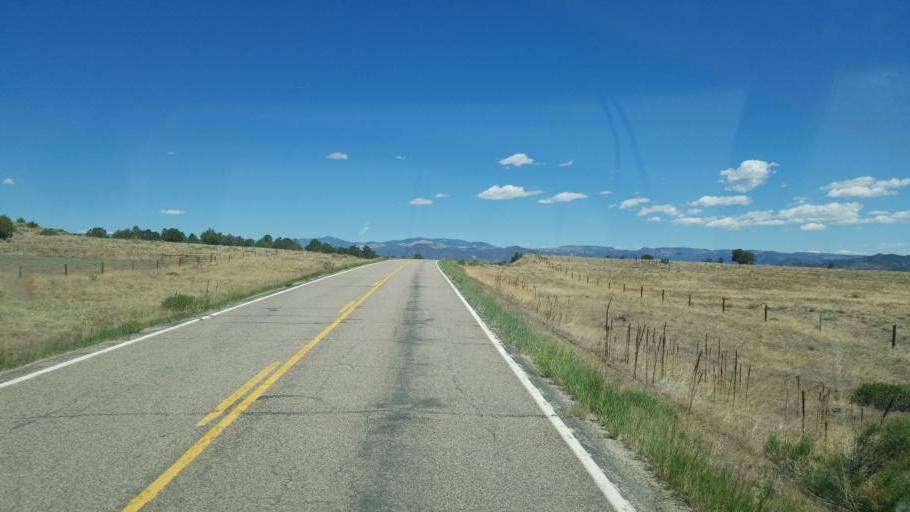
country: US
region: Colorado
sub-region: Custer County
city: Westcliffe
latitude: 38.2930
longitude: -105.6208
